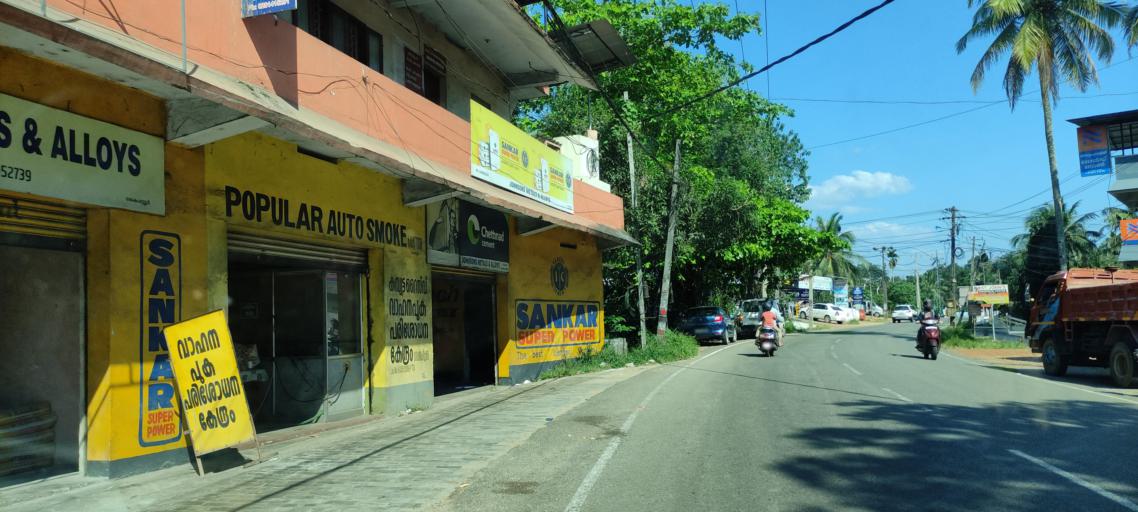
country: IN
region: Kerala
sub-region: Pattanamtitta
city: Pathanamthitta
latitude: 9.2321
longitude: 76.7516
